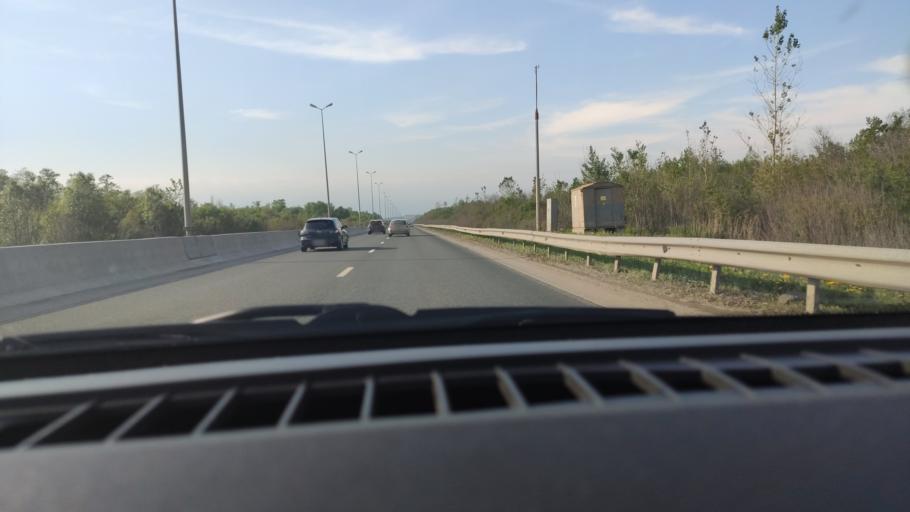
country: RU
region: Perm
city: Kondratovo
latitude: 57.9897
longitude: 56.0647
